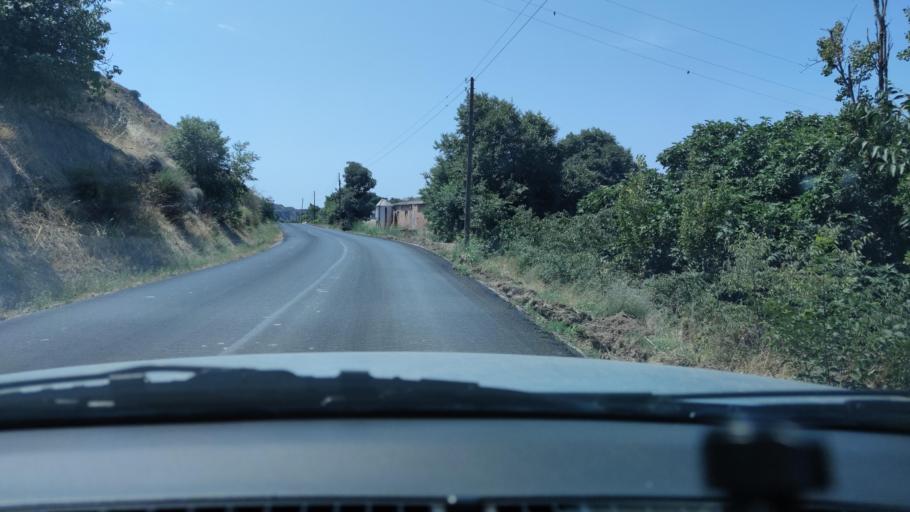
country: ES
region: Catalonia
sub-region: Provincia de Lleida
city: Alfarras
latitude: 41.8461
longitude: 0.5847
